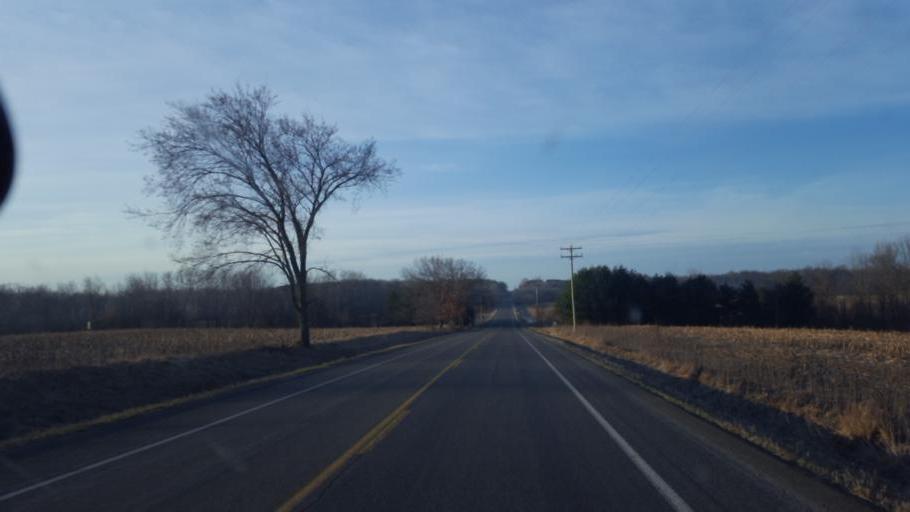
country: US
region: Michigan
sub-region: Montcalm County
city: Edmore
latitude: 43.4491
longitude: -85.0443
